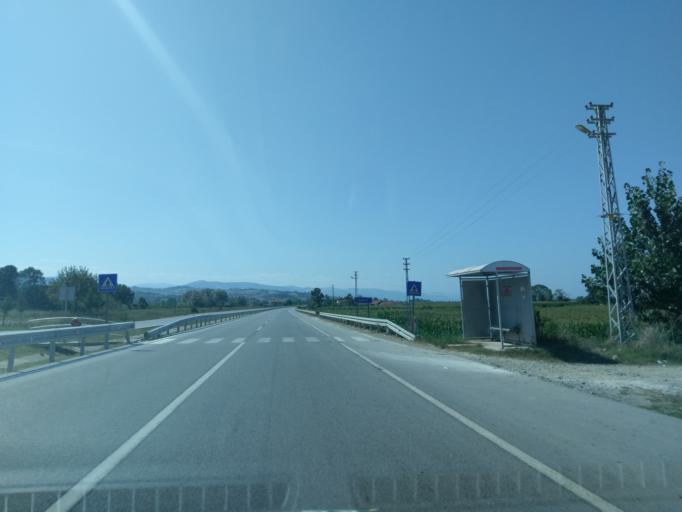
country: TR
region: Samsun
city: Alacam
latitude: 41.6084
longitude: 35.6708
